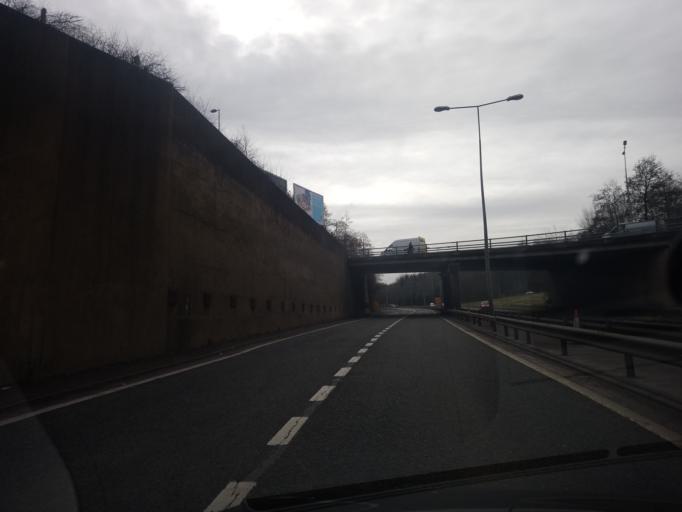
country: GB
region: England
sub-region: Telford and Wrekin
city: Oakengates
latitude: 52.6895
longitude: -2.4453
